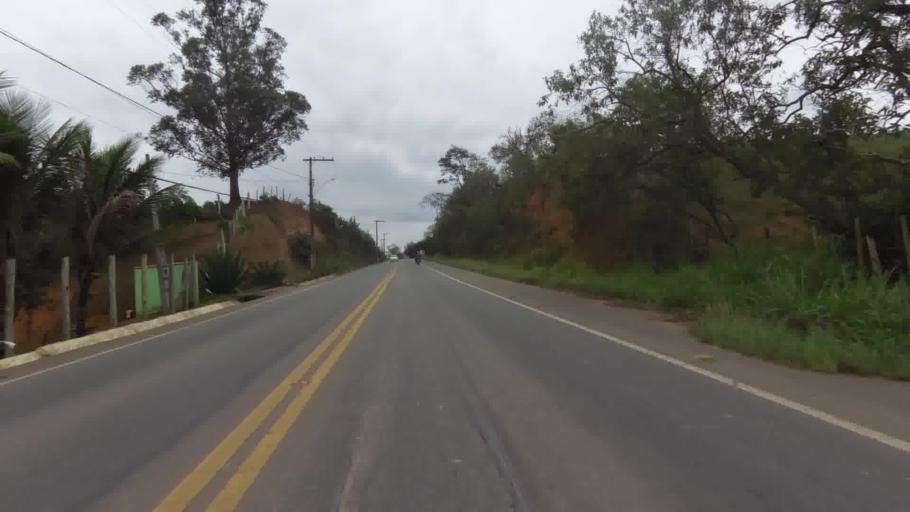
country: BR
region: Espirito Santo
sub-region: Piuma
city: Piuma
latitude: -20.8162
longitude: -40.7339
